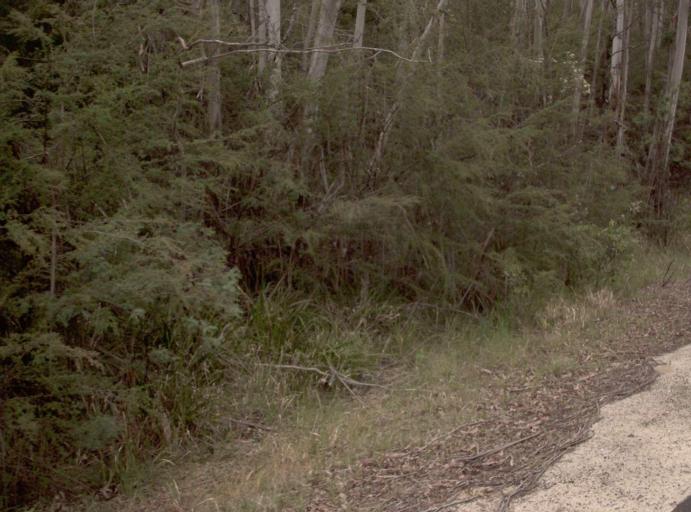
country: AU
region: New South Wales
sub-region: Bombala
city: Bombala
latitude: -37.3395
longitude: 149.2063
